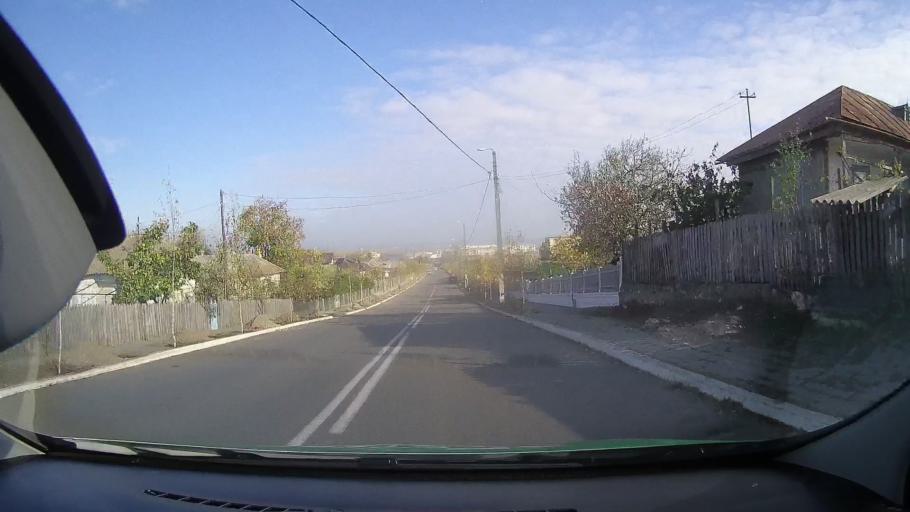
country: RO
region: Tulcea
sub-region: Comuna Mahmudia
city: Mahmudia
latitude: 45.0839
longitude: 29.0835
